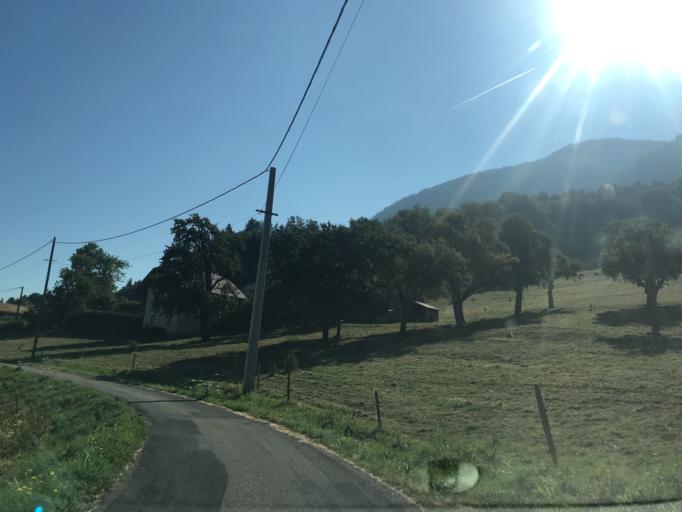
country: FR
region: Rhone-Alpes
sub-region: Departement de la Haute-Savoie
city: Thorens-Glieres
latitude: 45.9691
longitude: 6.2254
